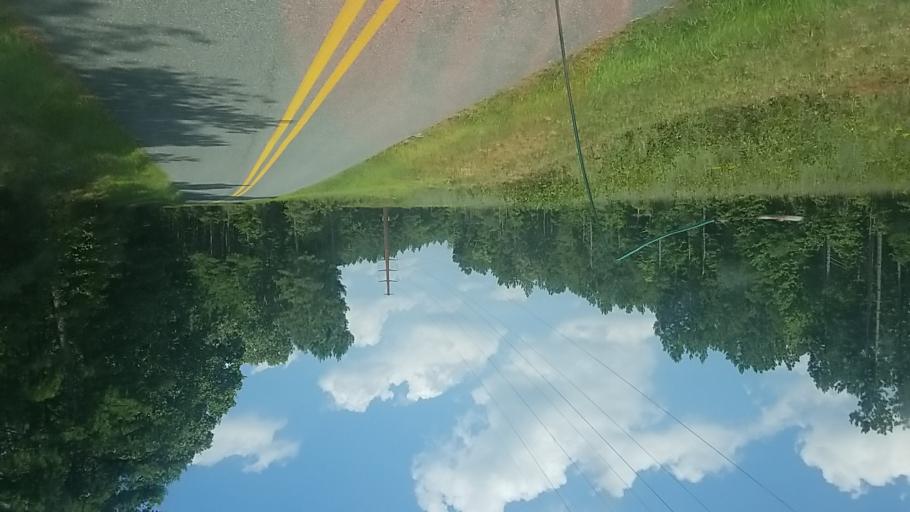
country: US
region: Maryland
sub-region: Worcester County
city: Snow Hill
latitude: 38.2775
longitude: -75.4747
